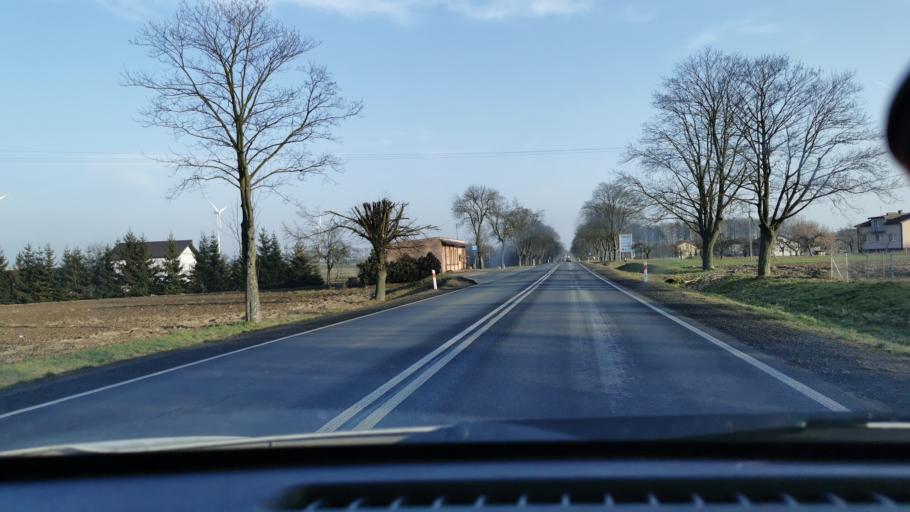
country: PL
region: Lodz Voivodeship
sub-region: Powiat sieradzki
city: Blaszki
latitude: 51.6369
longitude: 18.5215
